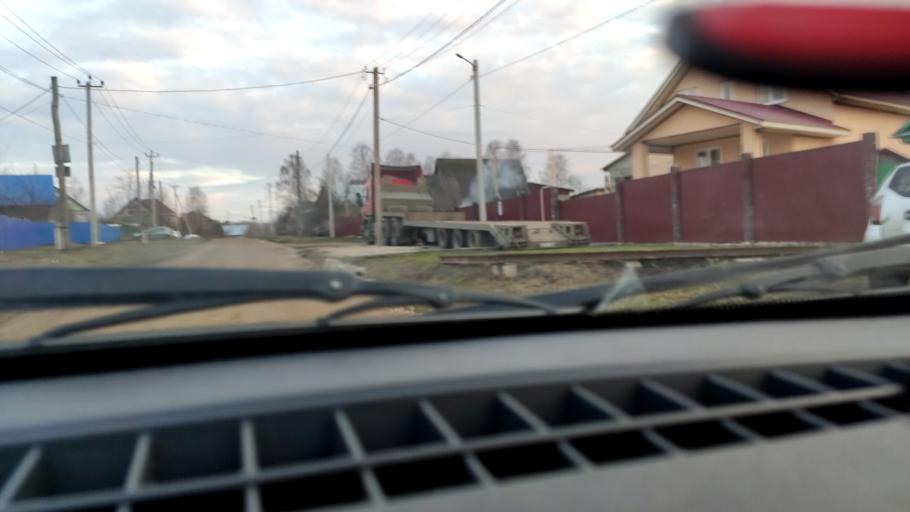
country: RU
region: Bashkortostan
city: Iglino
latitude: 54.8232
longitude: 56.3760
